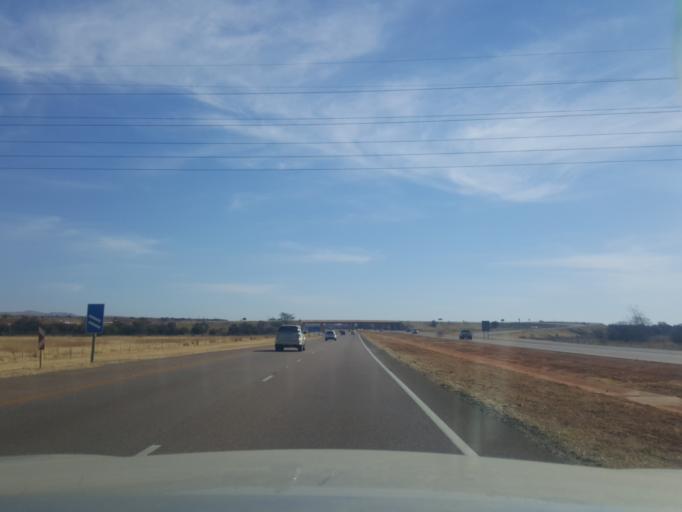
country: ZA
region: Gauteng
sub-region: City of Tshwane Metropolitan Municipality
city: Pretoria
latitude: -25.6465
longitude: 28.1582
